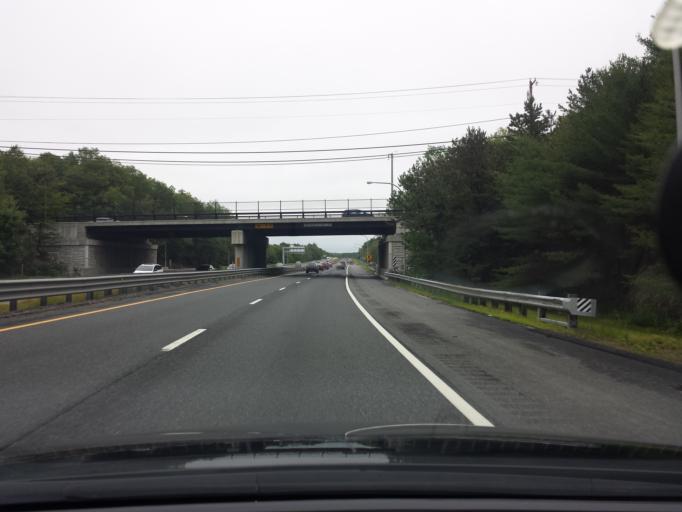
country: US
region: Rhode Island
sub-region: Kent County
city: West Greenwich
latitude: 41.6509
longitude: -71.6067
